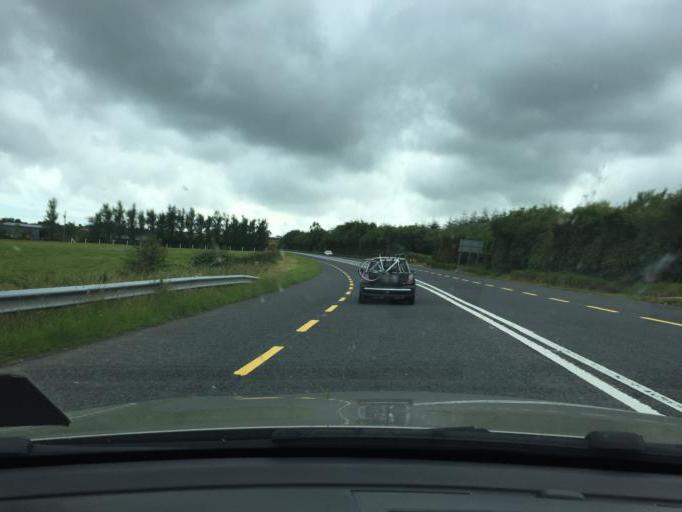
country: IE
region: Munster
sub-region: Waterford
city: Dungarvan
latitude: 52.1364
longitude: -7.5601
